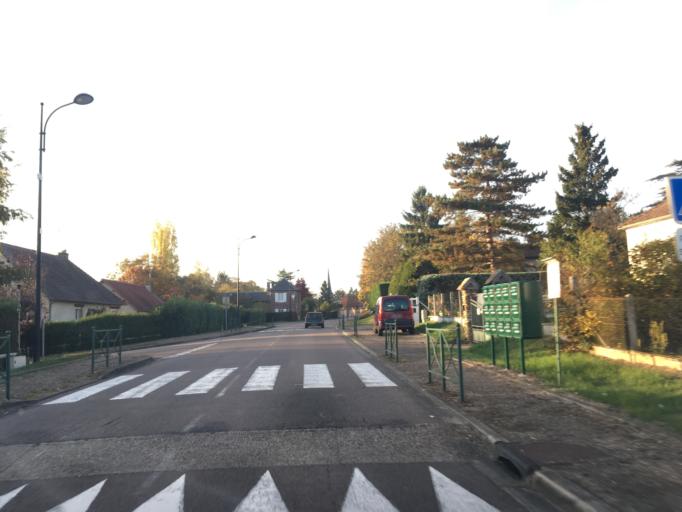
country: FR
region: Haute-Normandie
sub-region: Departement de l'Eure
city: Heudreville-sur-Eure
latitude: 49.1276
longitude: 1.2144
